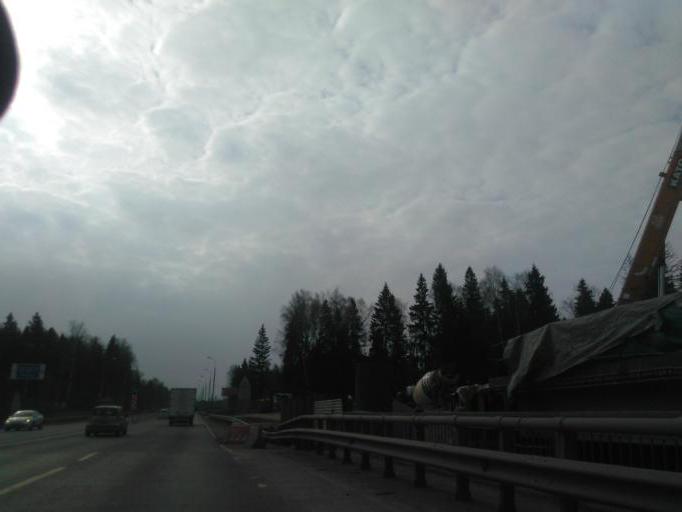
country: RU
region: Moskovskaya
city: Yermolino
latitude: 56.1371
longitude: 37.4974
